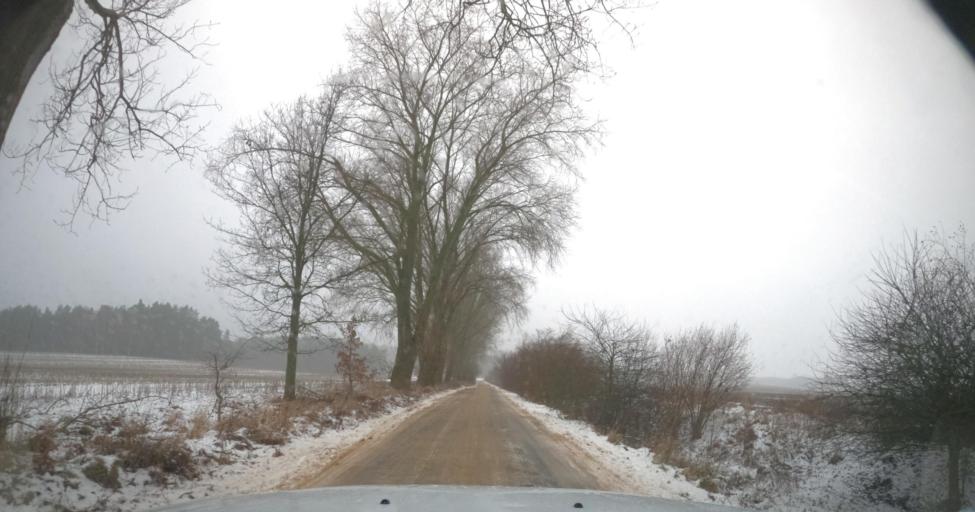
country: PL
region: West Pomeranian Voivodeship
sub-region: Powiat gryficki
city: Gryfice
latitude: 53.9002
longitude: 15.1307
